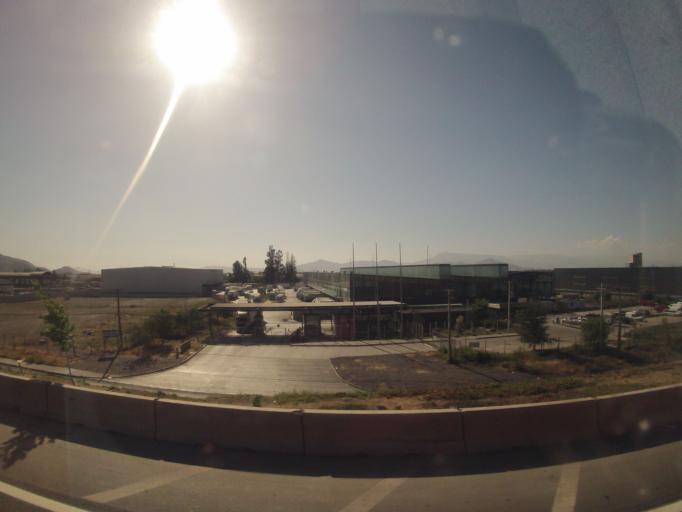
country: CL
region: Santiago Metropolitan
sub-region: Provincia de Maipo
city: San Bernardo
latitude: -33.5552
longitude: -70.7099
